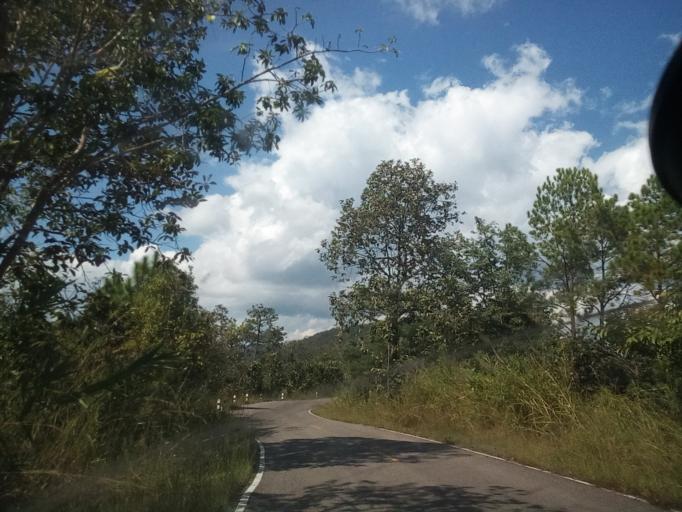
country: TH
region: Chiang Mai
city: Samoeng
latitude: 18.8641
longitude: 98.6948
